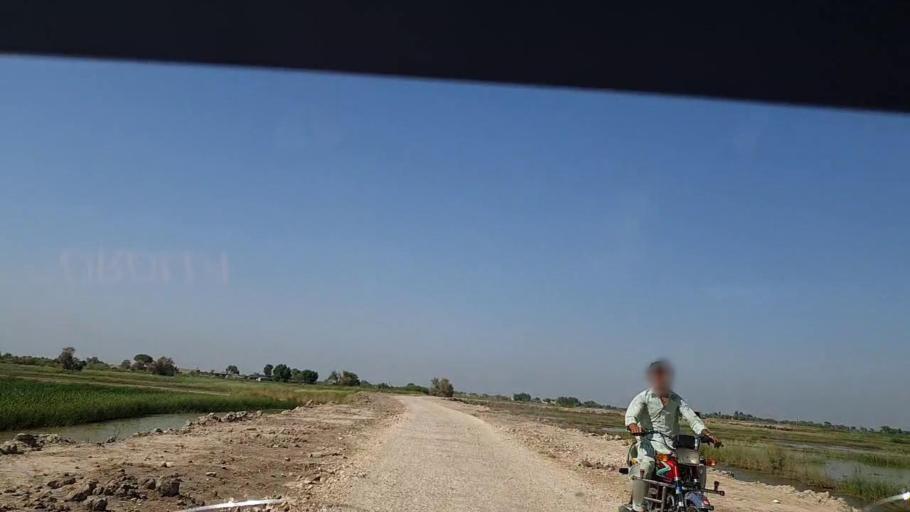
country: PK
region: Sindh
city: Tangwani
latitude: 28.3207
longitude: 69.0832
